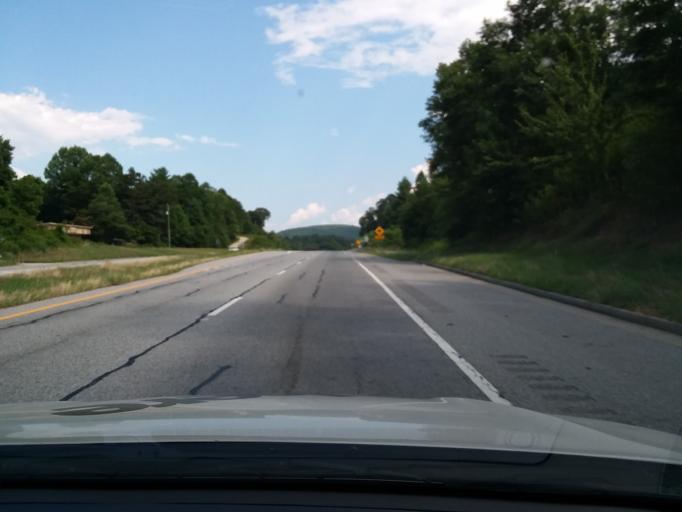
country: US
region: Georgia
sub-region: Rabun County
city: Clayton
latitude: 34.7890
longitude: -83.4074
